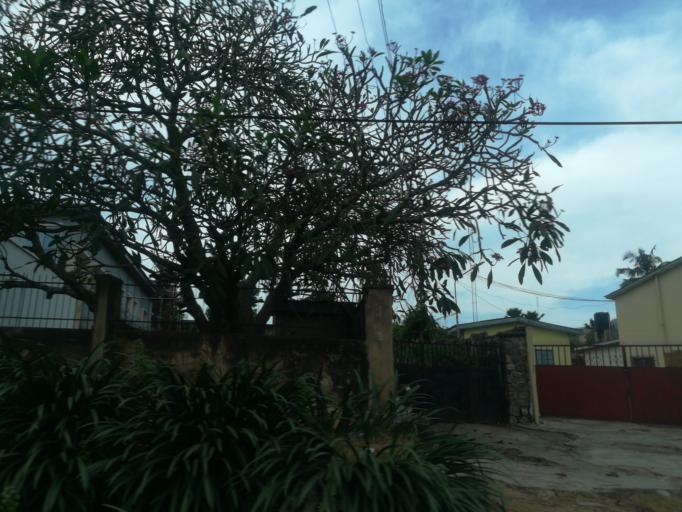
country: NG
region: Oyo
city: Ibadan
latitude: 7.4159
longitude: 3.9053
